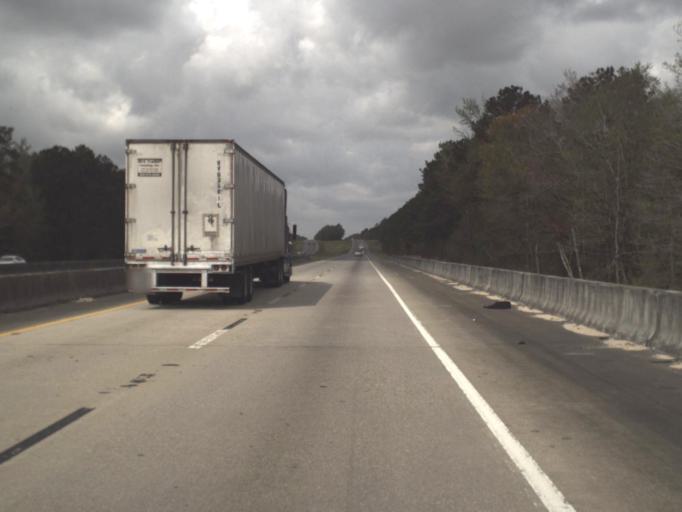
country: US
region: Florida
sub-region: Okaloosa County
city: Crestview
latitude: 30.7272
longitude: -86.5226
